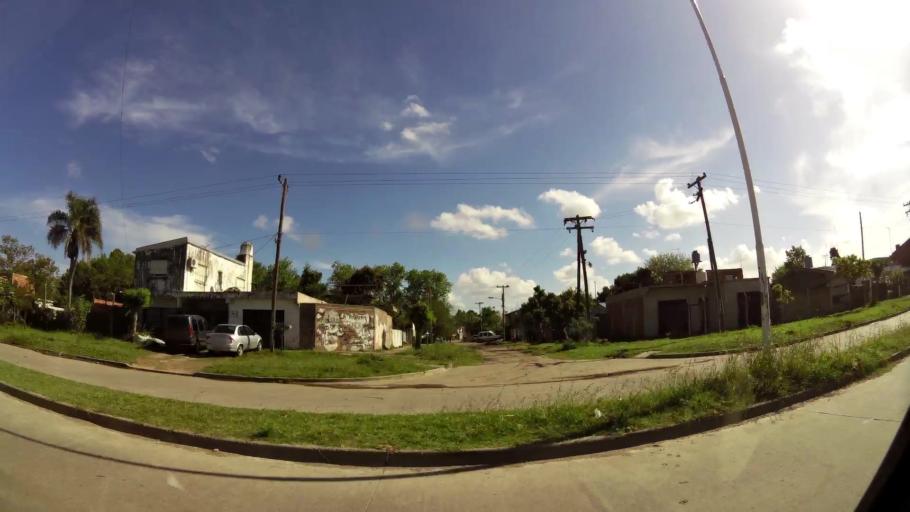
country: AR
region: Buenos Aires
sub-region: Partido de Quilmes
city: Quilmes
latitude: -34.8034
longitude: -58.2323
